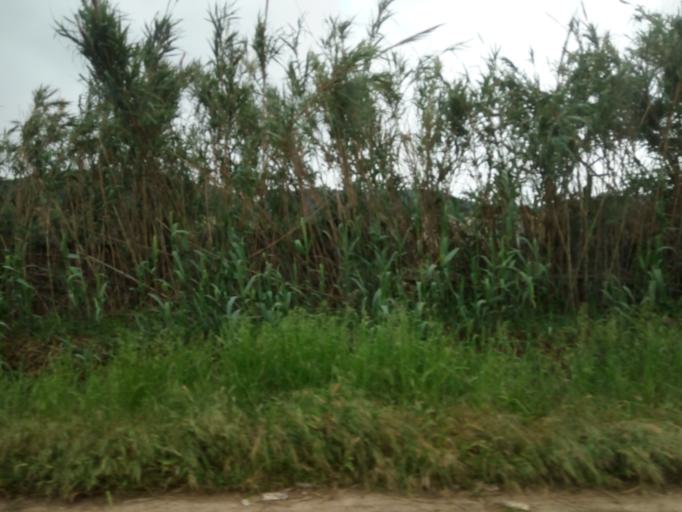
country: DZ
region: Tipaza
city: Tipasa
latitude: 36.5898
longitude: 2.5217
